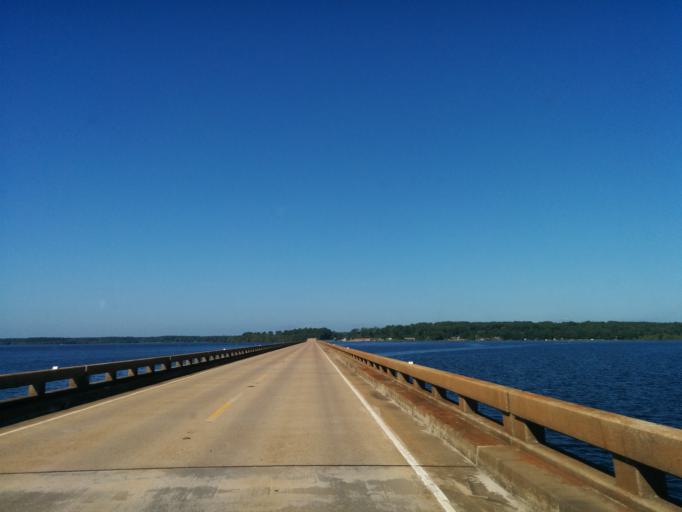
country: US
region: Texas
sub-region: Sabine County
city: Milam
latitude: 31.4713
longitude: -93.7371
